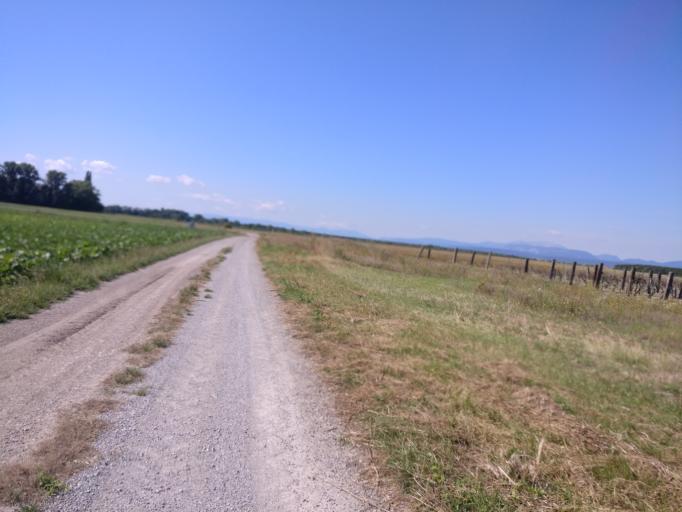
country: AT
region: Lower Austria
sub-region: Politischer Bezirk Baden
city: Pottendorf
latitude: 47.9161
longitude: 16.3574
